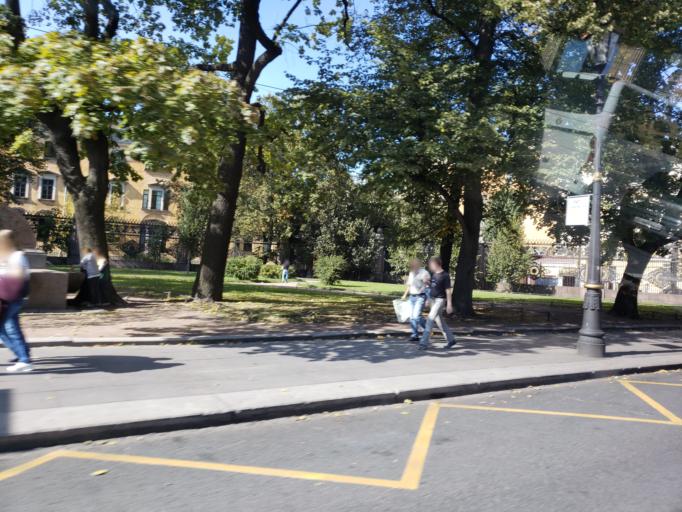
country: RU
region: St.-Petersburg
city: Saint Petersburg
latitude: 59.9345
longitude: 30.3233
